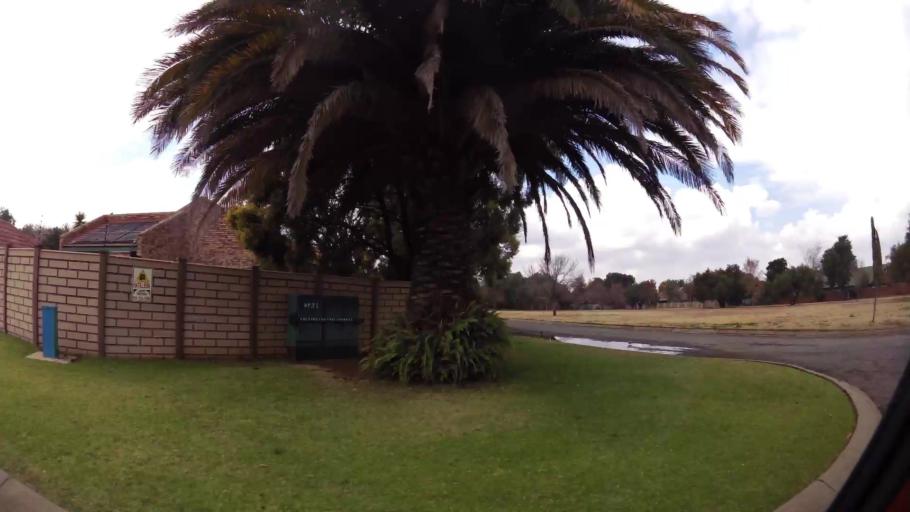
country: ZA
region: Gauteng
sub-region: Sedibeng District Municipality
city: Vanderbijlpark
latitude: -26.7344
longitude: 27.8500
